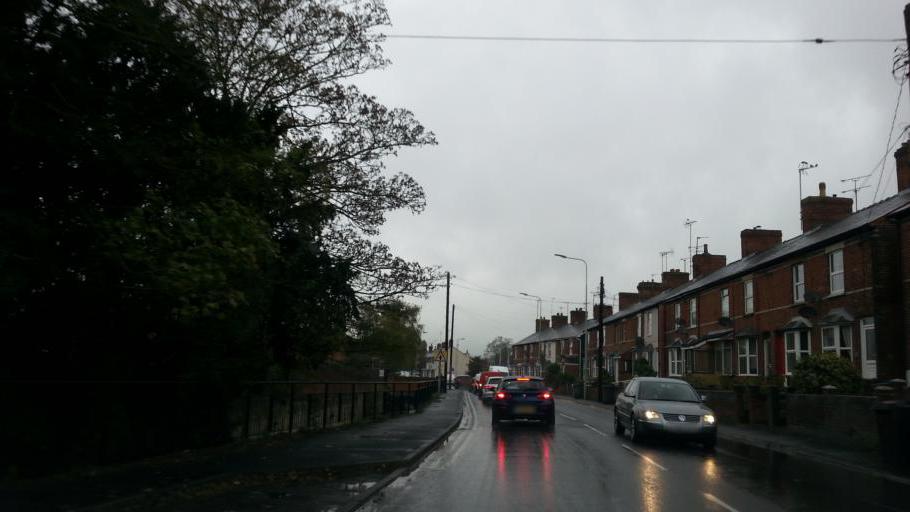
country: GB
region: England
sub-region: Suffolk
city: Haverhill
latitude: 52.0835
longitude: 0.4400
